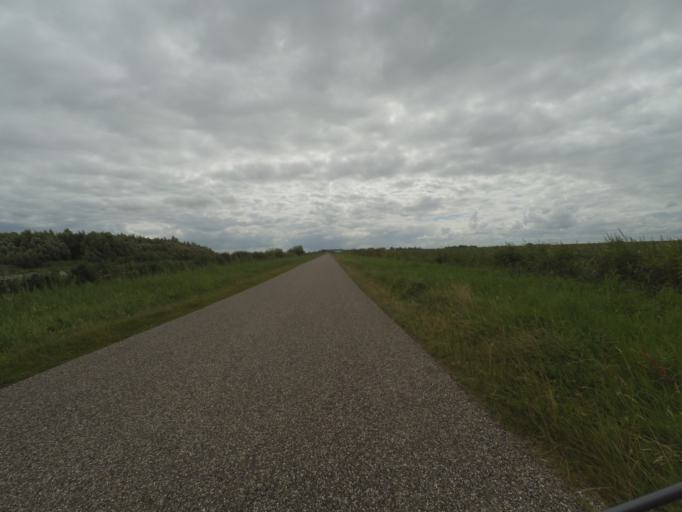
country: NL
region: Friesland
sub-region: Gemeente Dongeradeel
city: Anjum
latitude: 53.3494
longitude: 6.1530
